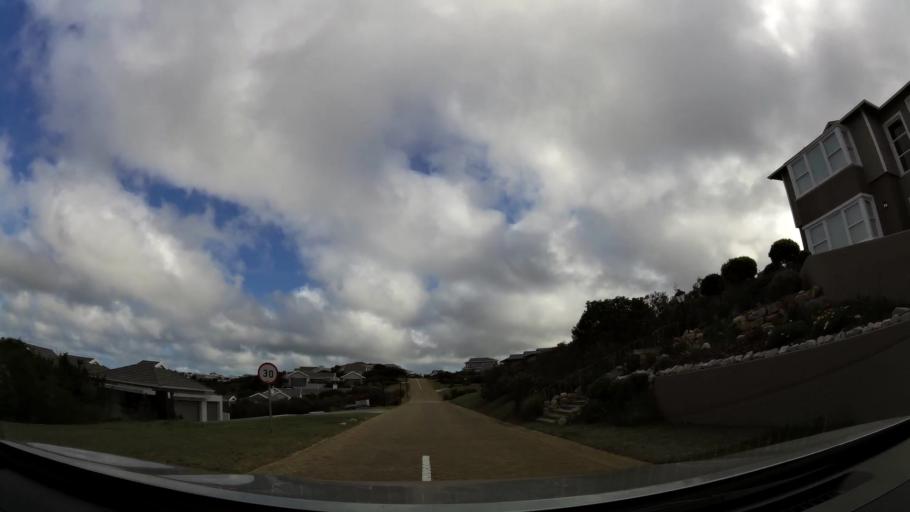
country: ZA
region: Western Cape
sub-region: Eden District Municipality
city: Plettenberg Bay
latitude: -34.0658
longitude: 23.3574
